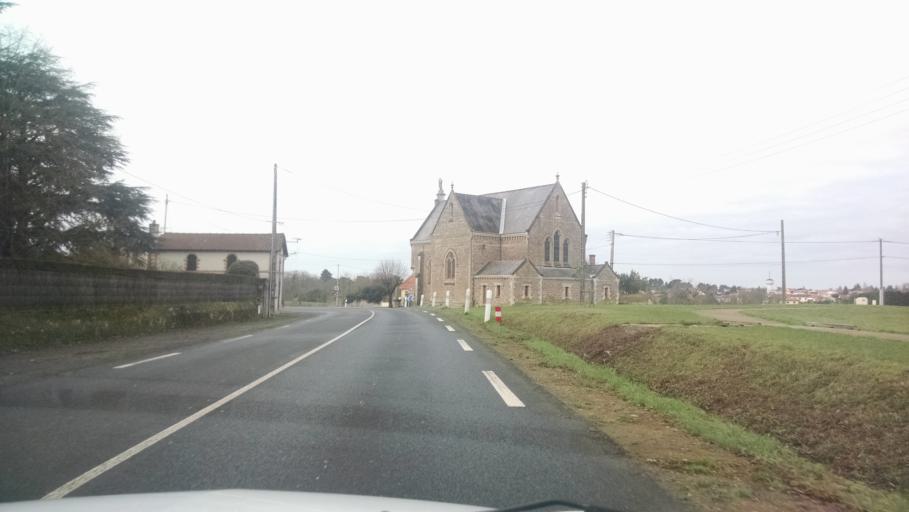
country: FR
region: Pays de la Loire
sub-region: Departement de la Loire-Atlantique
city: Clisson
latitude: 47.0862
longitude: -1.2671
